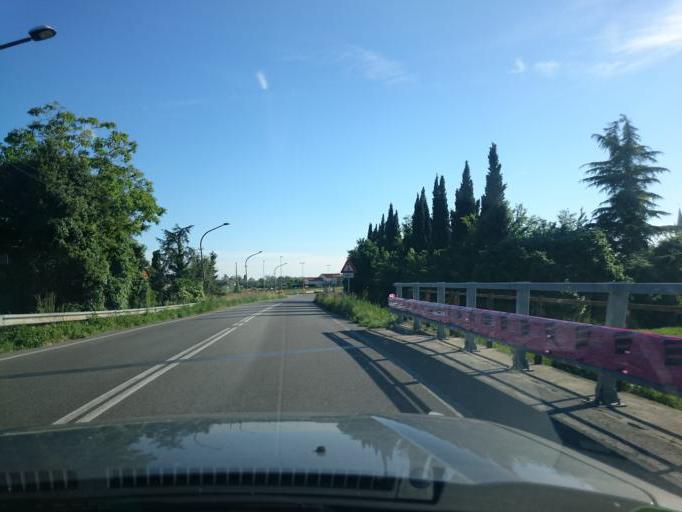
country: IT
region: Veneto
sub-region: Provincia di Venezia
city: Stigliano
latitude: 45.5267
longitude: 12.0498
